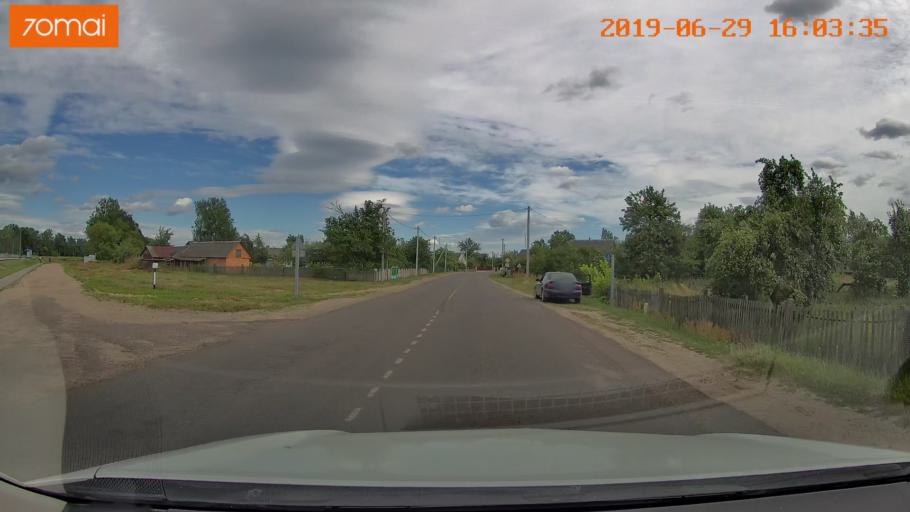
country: BY
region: Brest
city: Luninyets
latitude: 52.2288
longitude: 27.0201
